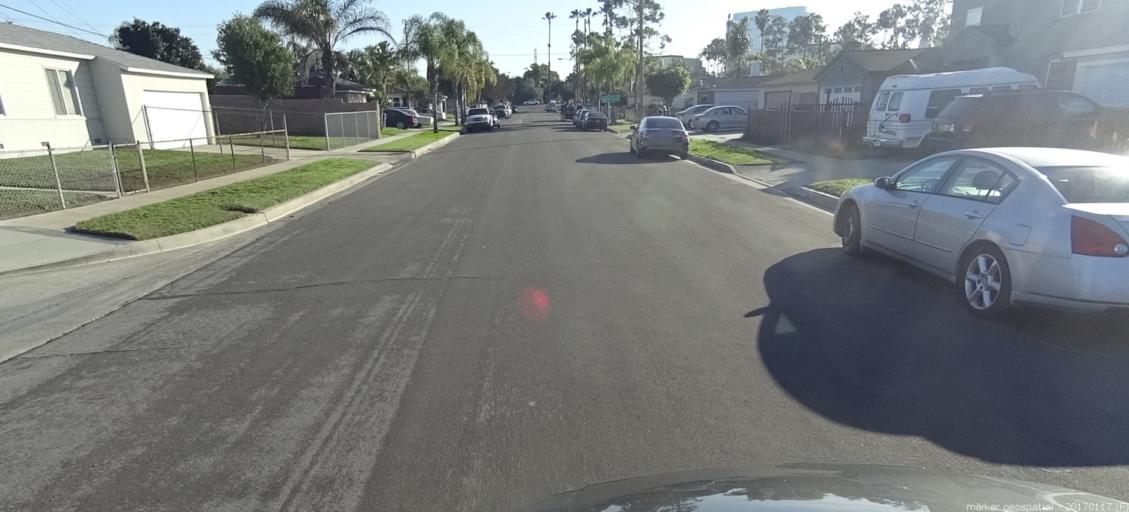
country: US
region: California
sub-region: Orange County
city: Midway City
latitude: 33.7391
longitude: -117.9934
